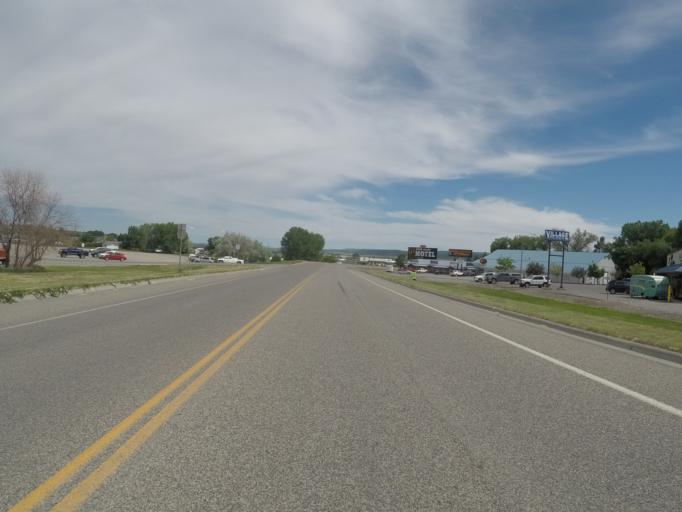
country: US
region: Montana
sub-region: Stillwater County
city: Columbus
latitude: 45.6434
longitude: -109.2478
